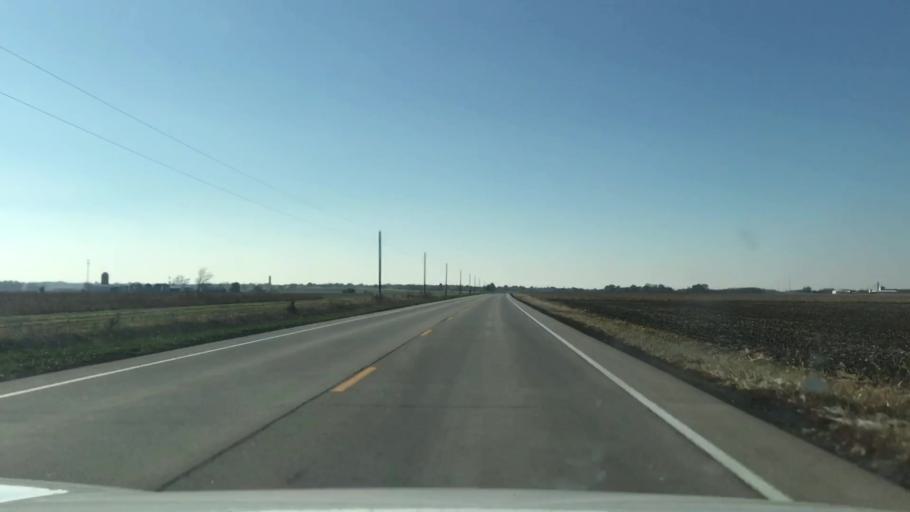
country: US
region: Illinois
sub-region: Washington County
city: Okawville
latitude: 38.4426
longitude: -89.5122
